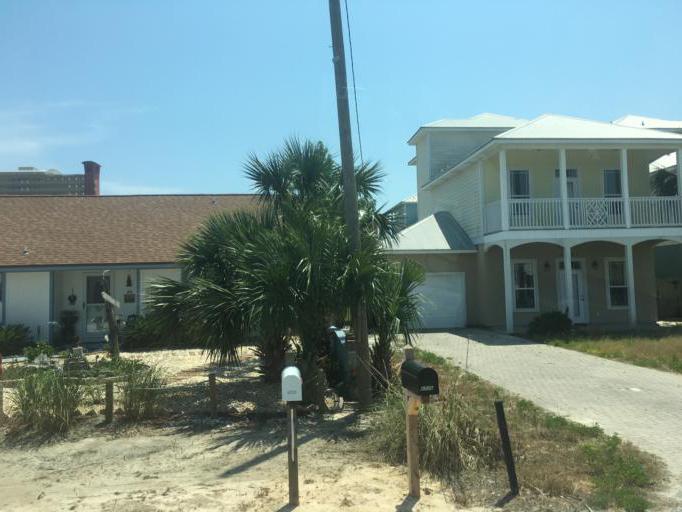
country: US
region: Florida
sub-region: Bay County
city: Lower Grand Lagoon
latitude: 30.1561
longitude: -85.7686
